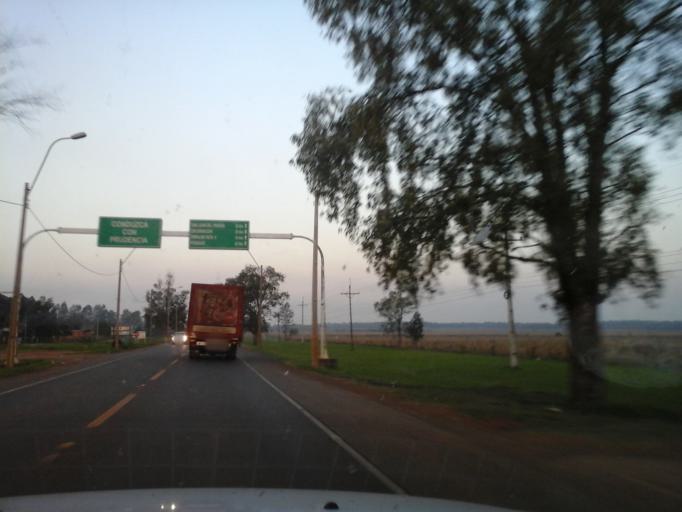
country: PY
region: Itapua
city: Carmen del Parana
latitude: -27.2202
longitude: -56.1344
